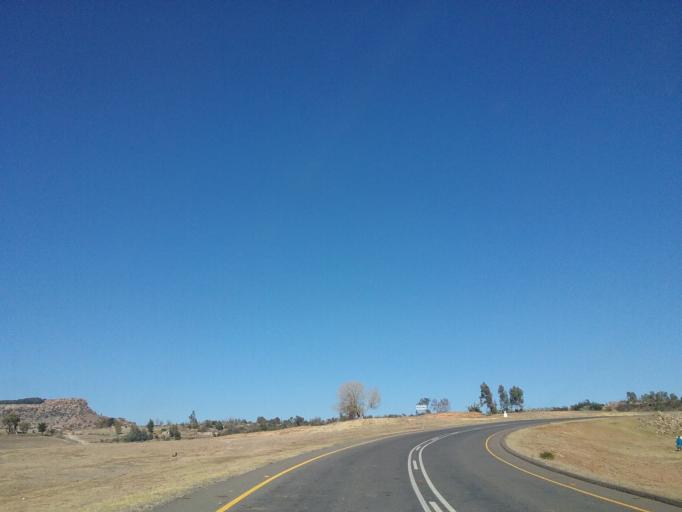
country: LS
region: Maseru
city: Nako
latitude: -29.4614
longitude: 27.6472
